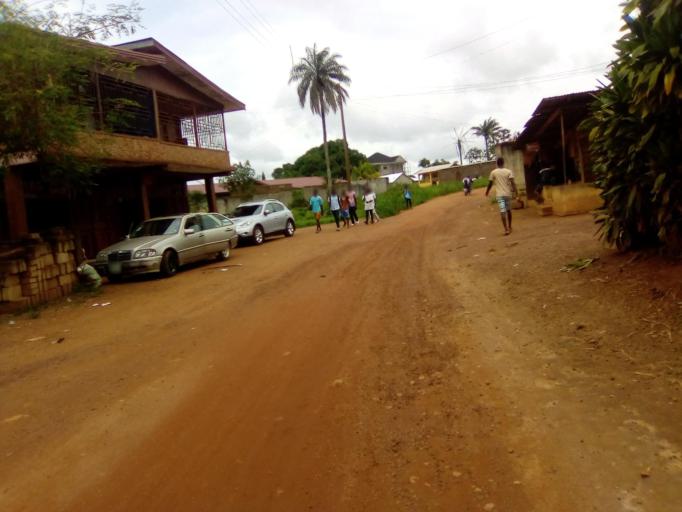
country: SL
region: Southern Province
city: Bo
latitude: 7.9473
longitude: -11.7189
